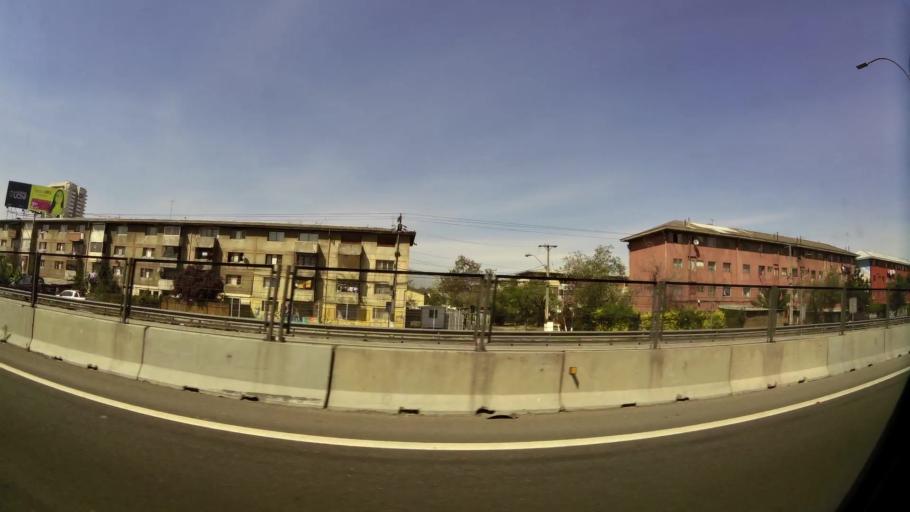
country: CL
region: Santiago Metropolitan
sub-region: Provincia de Santiago
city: Santiago
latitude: -33.4986
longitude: -70.6654
